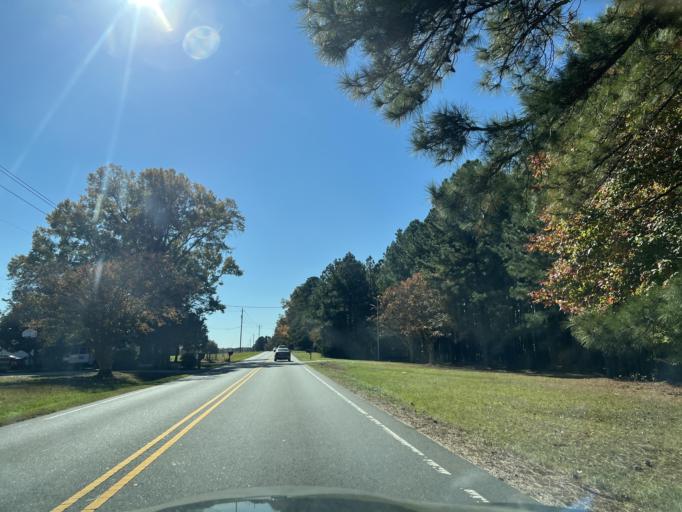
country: US
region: North Carolina
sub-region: Wake County
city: West Raleigh
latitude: 35.7384
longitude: -78.6815
